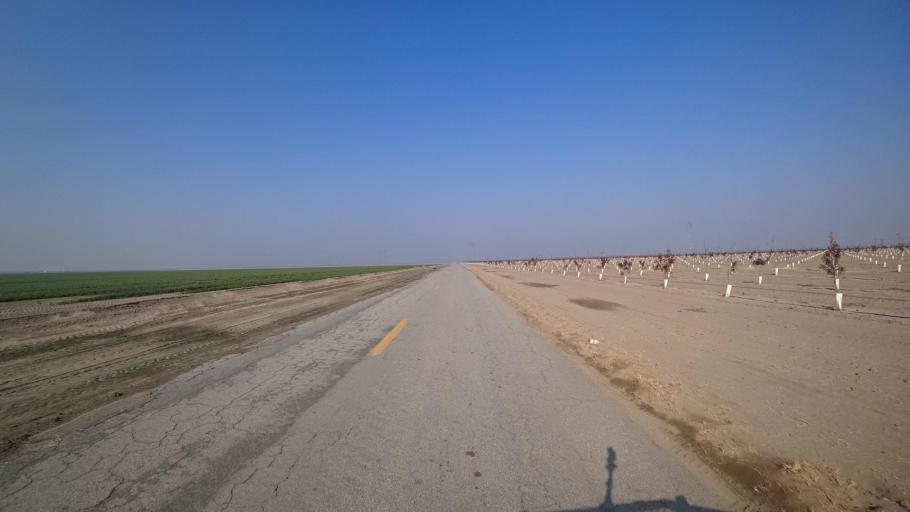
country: US
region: California
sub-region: Kern County
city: Greenfield
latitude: 35.1639
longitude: -119.0393
